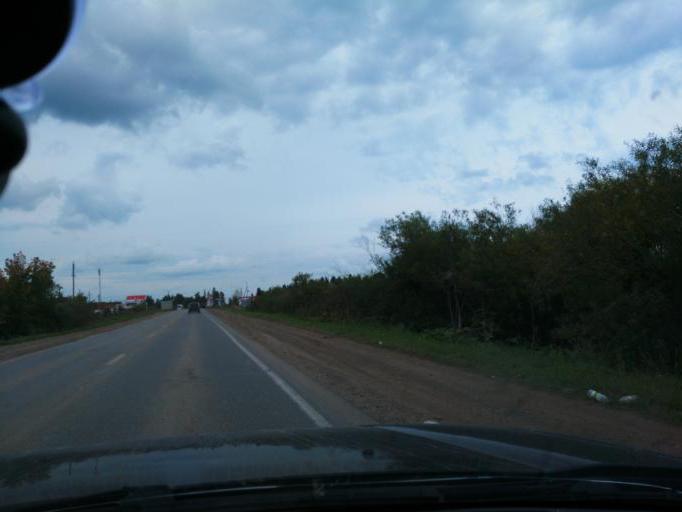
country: RU
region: Perm
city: Chernushka
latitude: 56.5327
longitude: 56.0863
